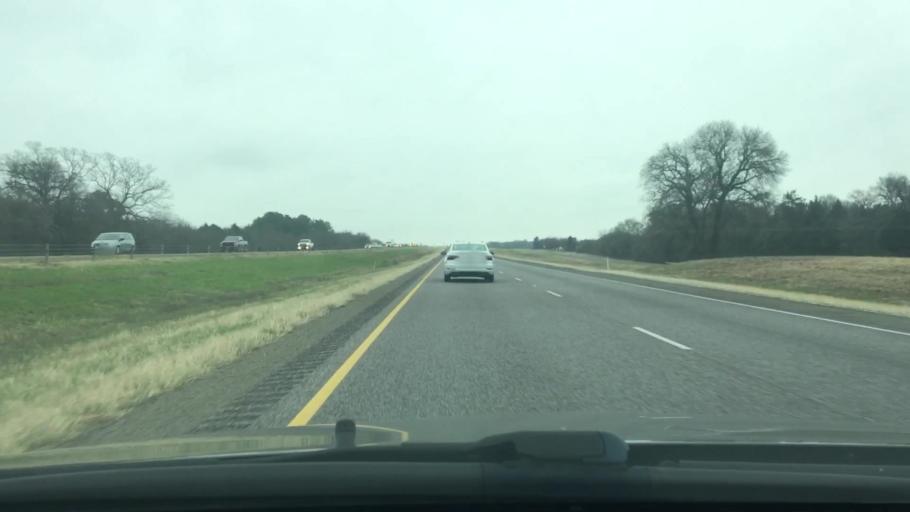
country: US
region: Texas
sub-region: Freestone County
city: Fairfield
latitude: 31.7773
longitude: -96.2284
